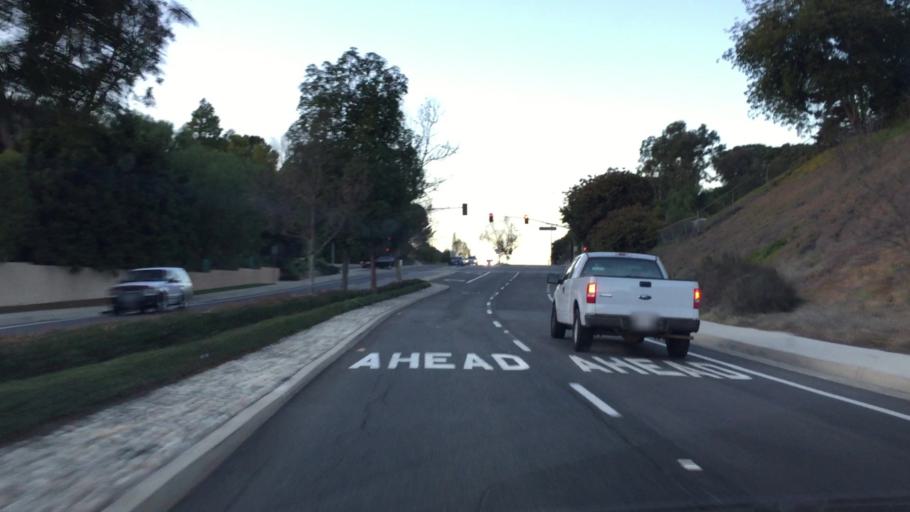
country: US
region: California
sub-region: Orange County
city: Laguna Niguel
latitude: 33.5216
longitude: -117.7070
